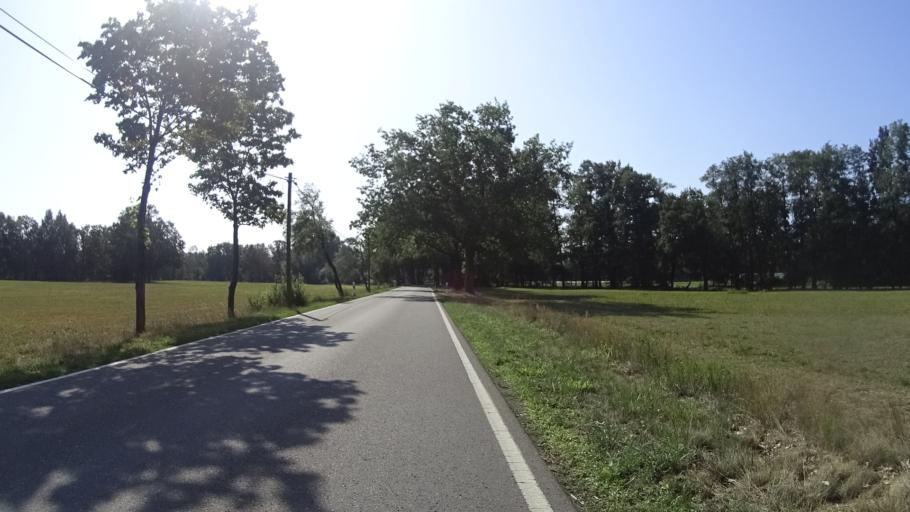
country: DE
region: Brandenburg
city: Burg
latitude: 51.8513
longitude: 14.1357
